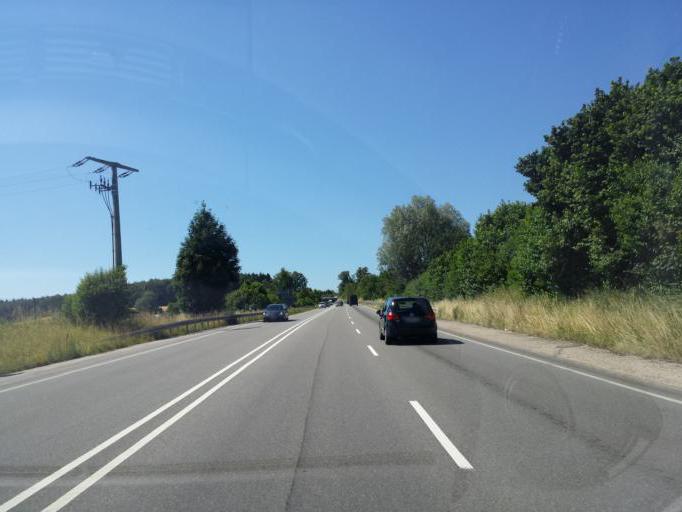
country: DE
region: Baden-Wuerttemberg
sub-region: Tuebingen Region
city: Owingen
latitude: 47.7956
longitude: 9.1416
